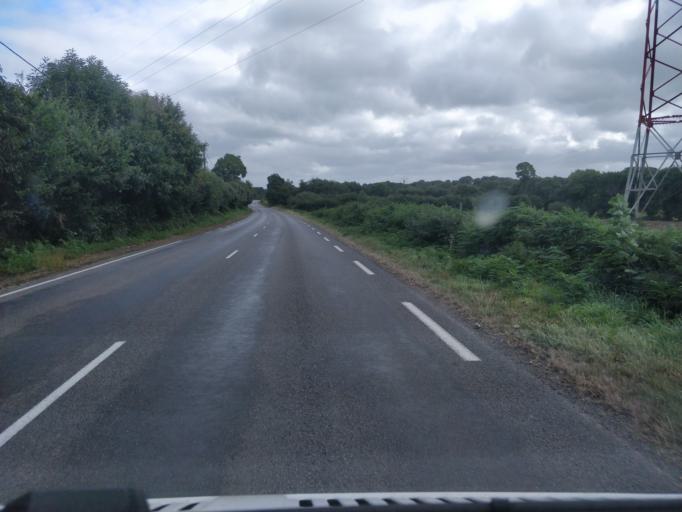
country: FR
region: Brittany
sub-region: Departement du Finistere
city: Ploneis
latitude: 47.9921
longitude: -4.2199
